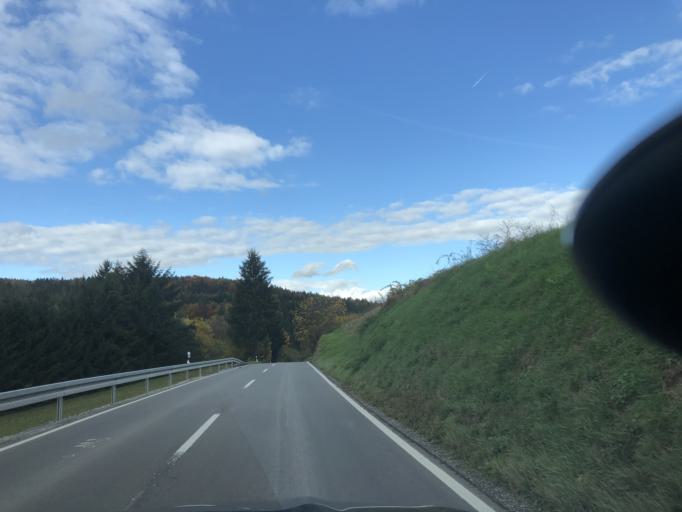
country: DE
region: Baden-Wuerttemberg
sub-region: Regierungsbezirk Stuttgart
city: Winterbach
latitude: 48.8308
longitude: 9.4552
